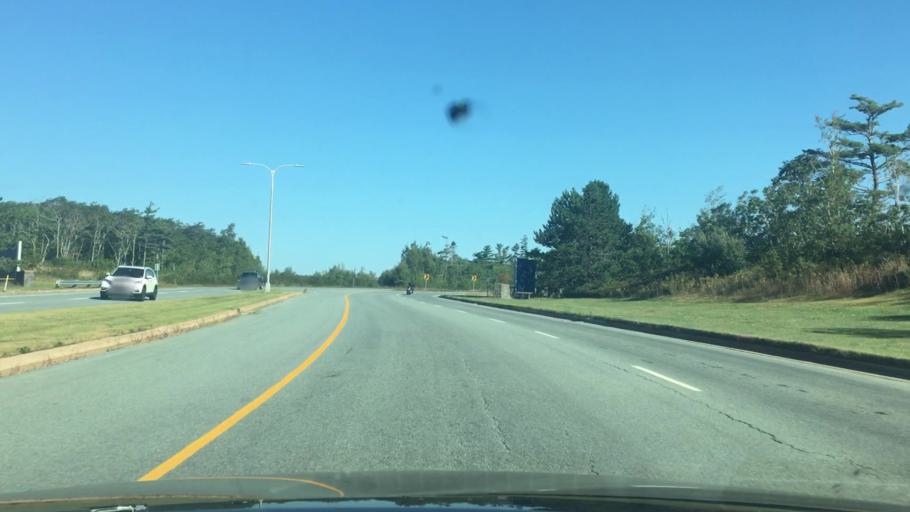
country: CA
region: Nova Scotia
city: Dartmouth
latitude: 44.7201
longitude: -63.5805
